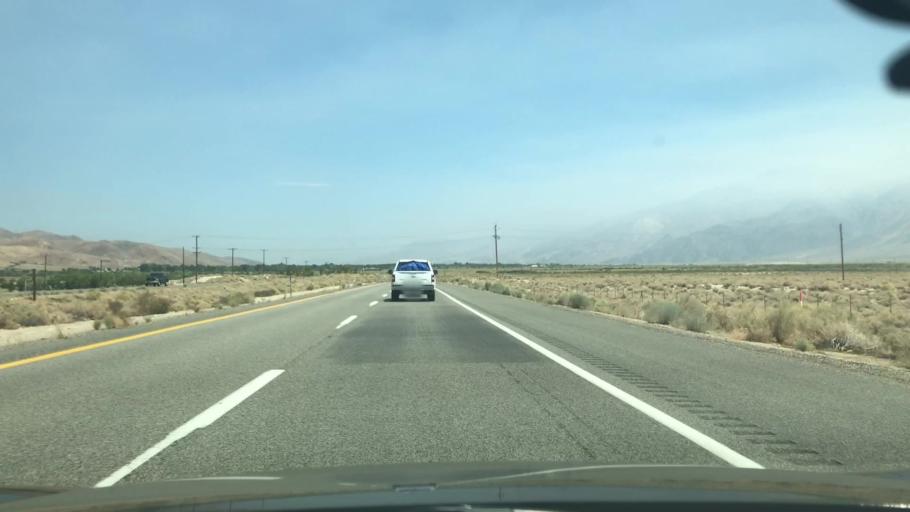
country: US
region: California
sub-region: Inyo County
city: Lone Pine
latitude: 36.5518
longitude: -118.0488
